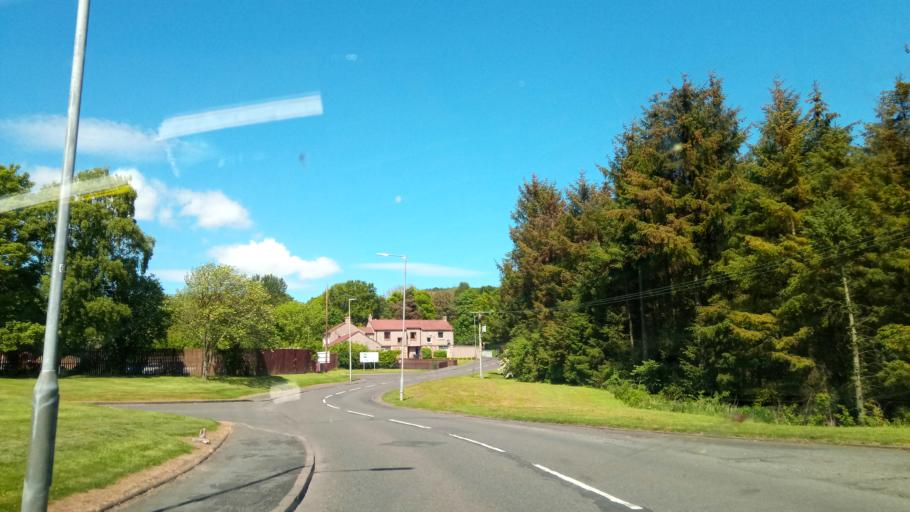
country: GB
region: Scotland
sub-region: The Scottish Borders
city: Hawick
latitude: 55.4369
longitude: -2.7594
